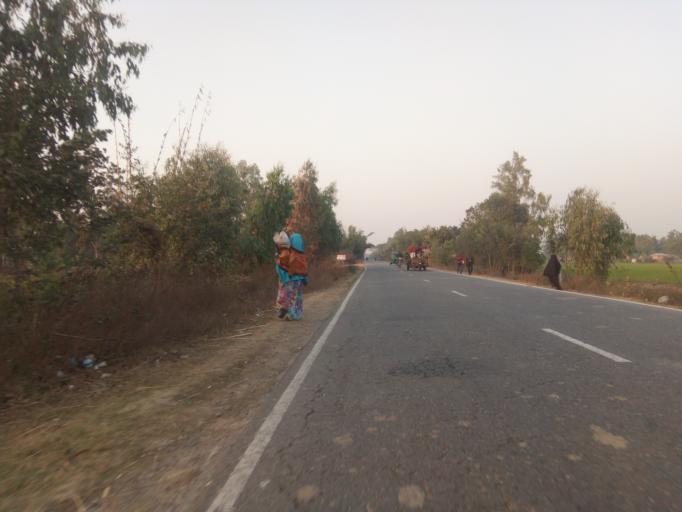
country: BD
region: Rajshahi
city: Bogra
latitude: 24.6018
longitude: 89.2396
